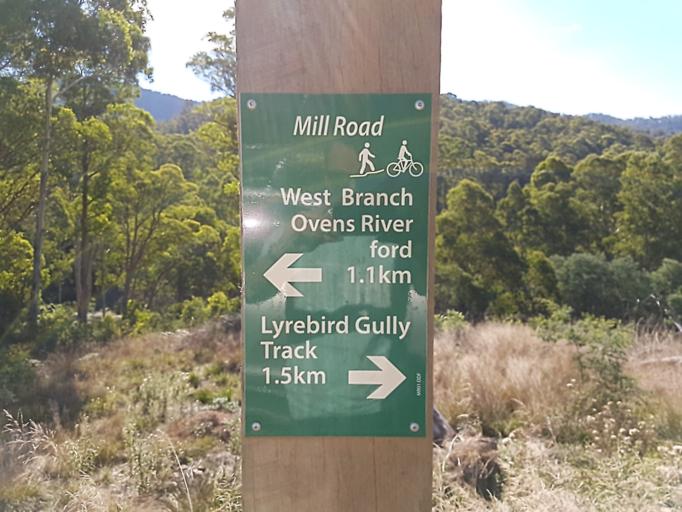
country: AU
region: Victoria
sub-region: Alpine
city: Mount Beauty
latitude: -36.9126
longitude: 147.0478
